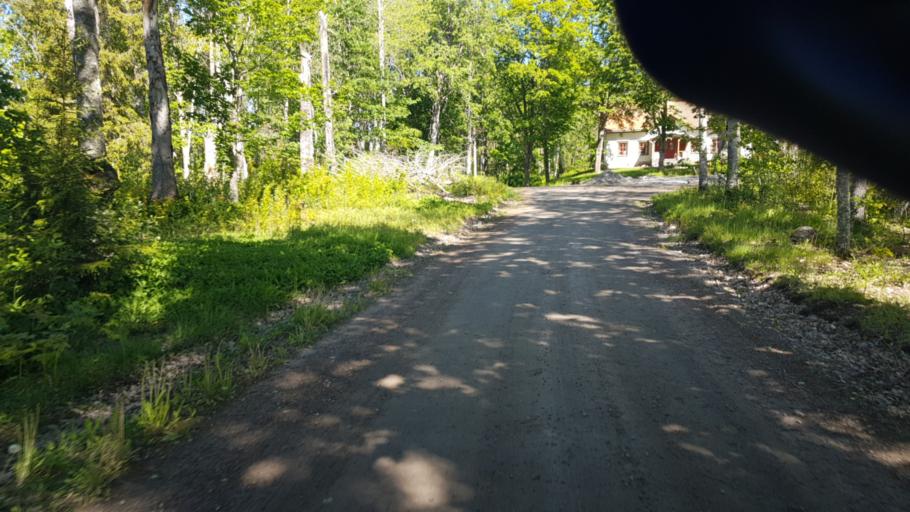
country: SE
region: Vaermland
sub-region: Grums Kommun
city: Grums
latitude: 59.4889
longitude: 12.9292
